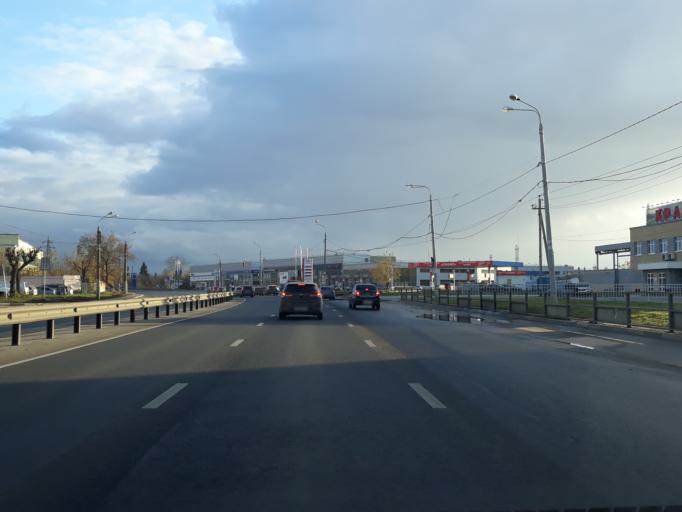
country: RU
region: Nizjnij Novgorod
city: Nizhniy Novgorod
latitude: 56.3117
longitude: 43.8993
